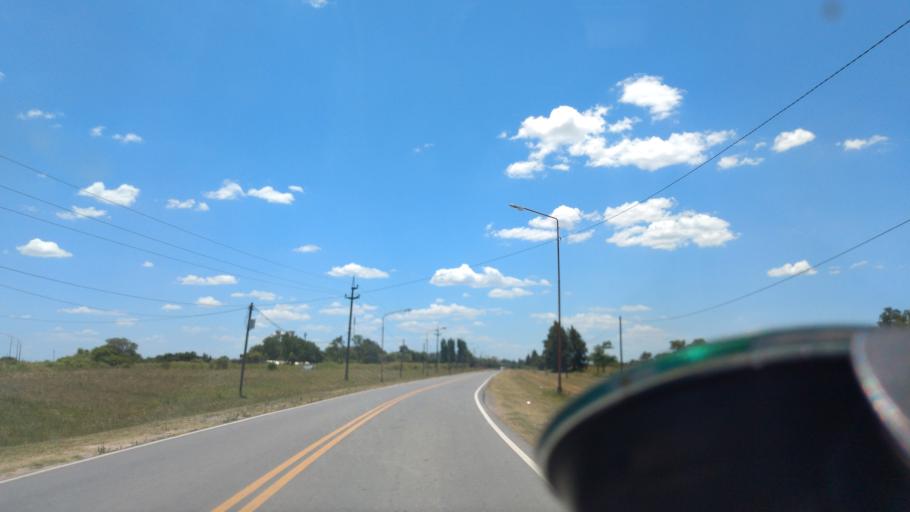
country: AR
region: Santa Fe
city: Laguna Paiva
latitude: -31.3265
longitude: -60.6591
